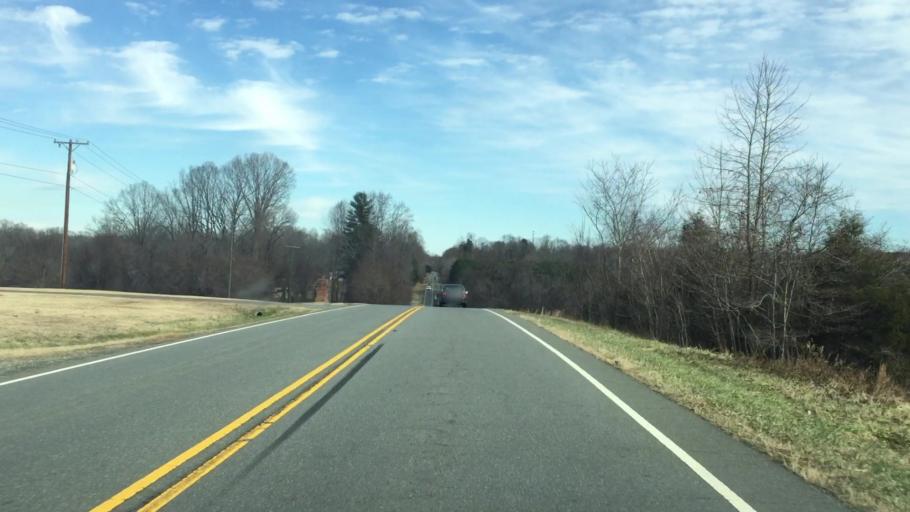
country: US
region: North Carolina
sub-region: Forsyth County
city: Walkertown
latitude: 36.2036
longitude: -80.0756
